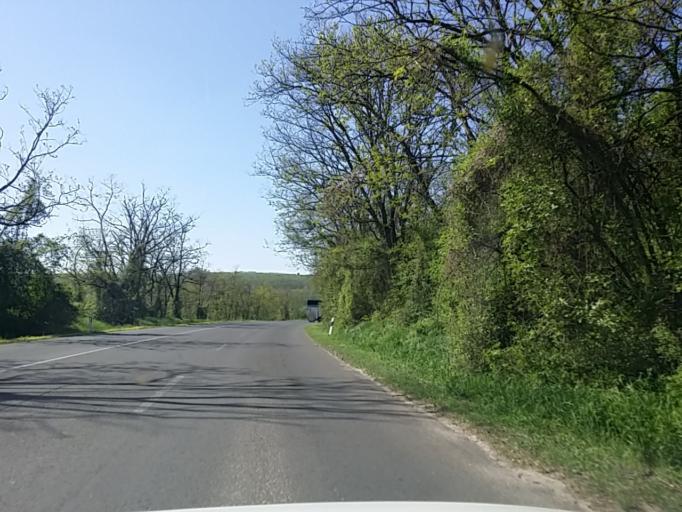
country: HU
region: Pest
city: Bag
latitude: 47.6366
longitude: 19.4613
